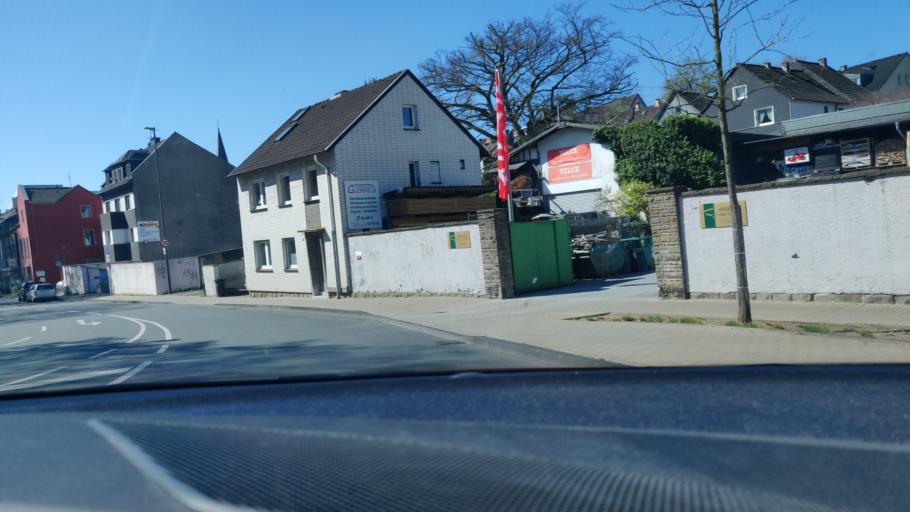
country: DE
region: North Rhine-Westphalia
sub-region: Regierungsbezirk Dusseldorf
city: Mettmann
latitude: 51.2540
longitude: 6.9784
